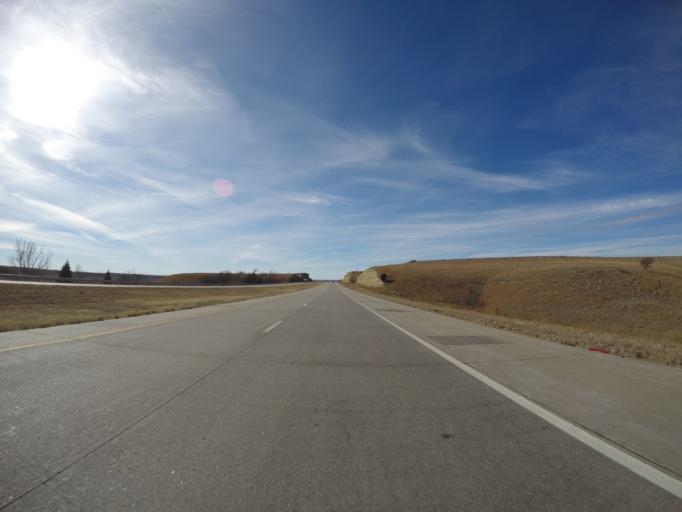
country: US
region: Kansas
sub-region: Riley County
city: Ogden
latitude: 39.0645
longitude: -96.6973
